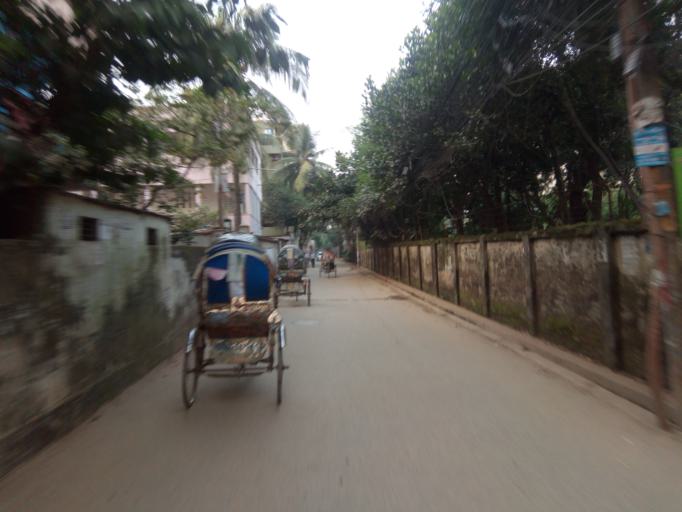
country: BD
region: Dhaka
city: Paltan
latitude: 23.7835
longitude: 90.3998
